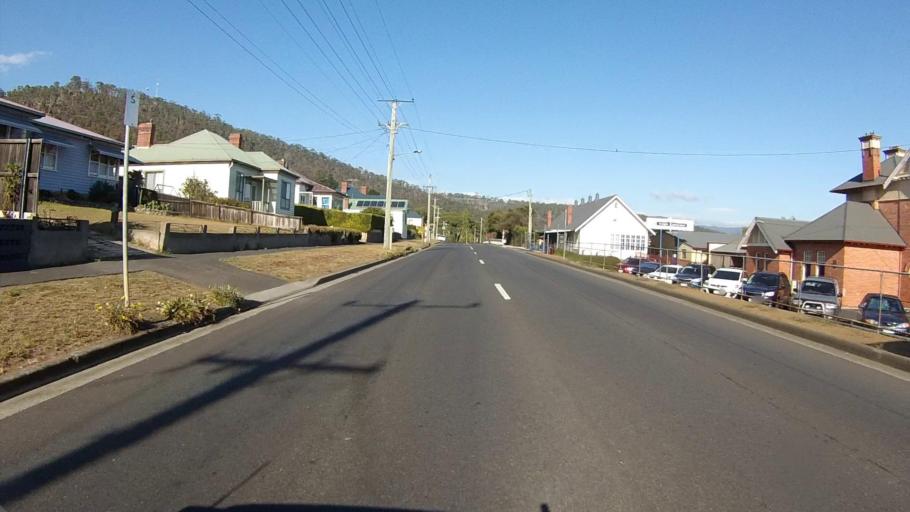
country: AU
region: Tasmania
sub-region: Derwent Valley
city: New Norfolk
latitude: -42.7806
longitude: 147.0568
